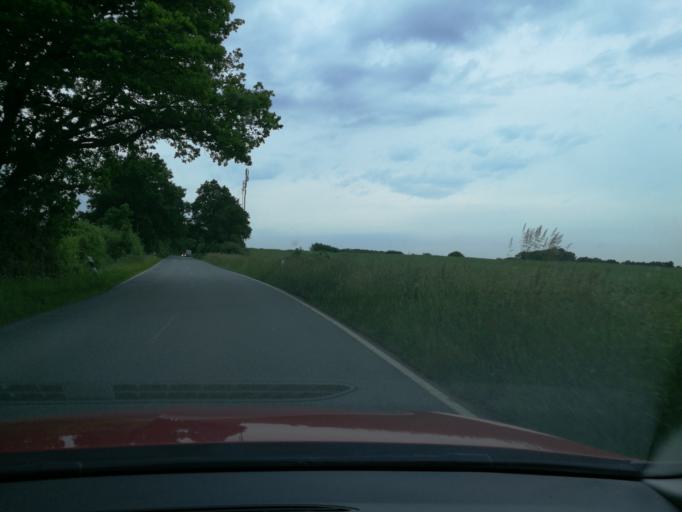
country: DE
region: Schleswig-Holstein
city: Todendorf
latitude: 53.7214
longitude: 10.3453
